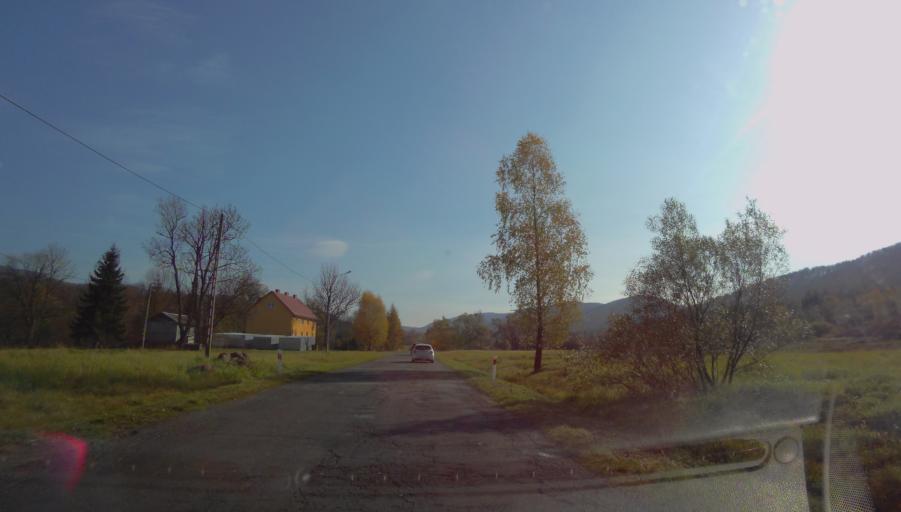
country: PL
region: Subcarpathian Voivodeship
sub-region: Powiat sanocki
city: Rzepedz
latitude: 49.2278
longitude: 22.1702
